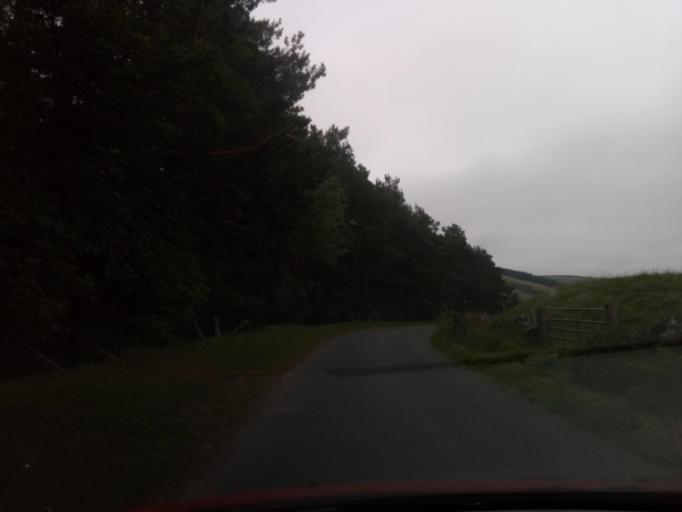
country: GB
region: Scotland
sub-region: The Scottish Borders
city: Galashiels
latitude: 55.7303
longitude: -2.8984
